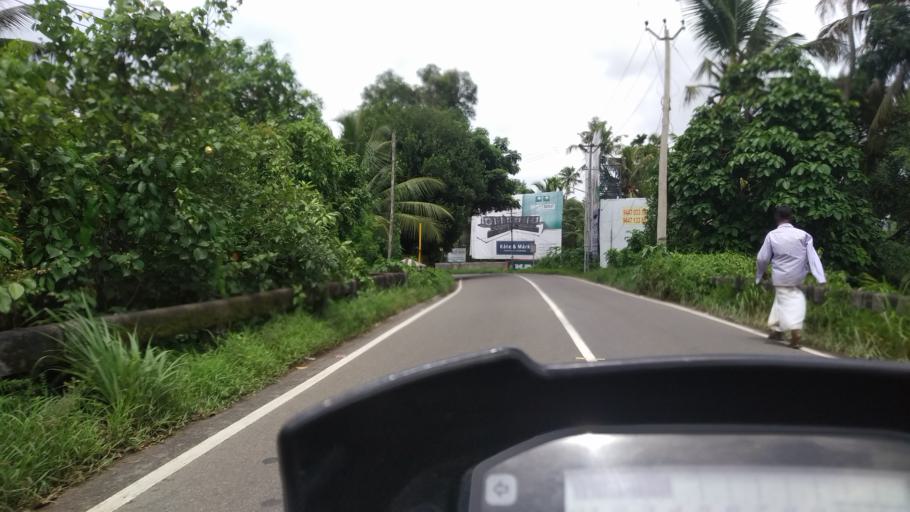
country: IN
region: Kerala
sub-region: Ernakulam
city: Aluva
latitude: 10.1298
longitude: 76.2938
